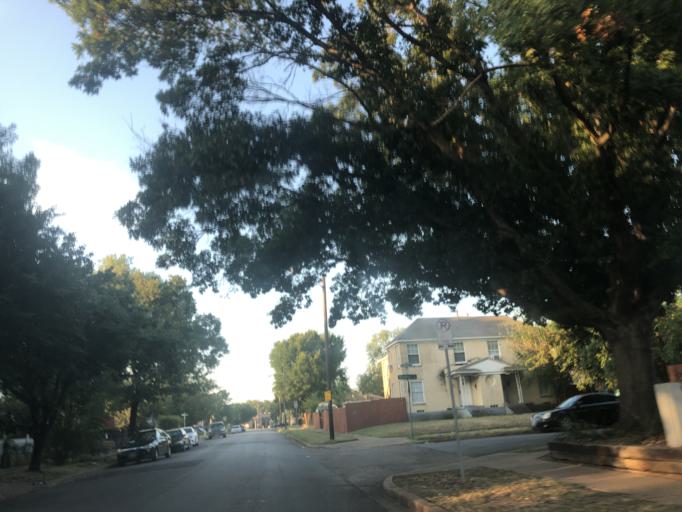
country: US
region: Texas
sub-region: Dallas County
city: Dallas
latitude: 32.7516
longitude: -96.8316
